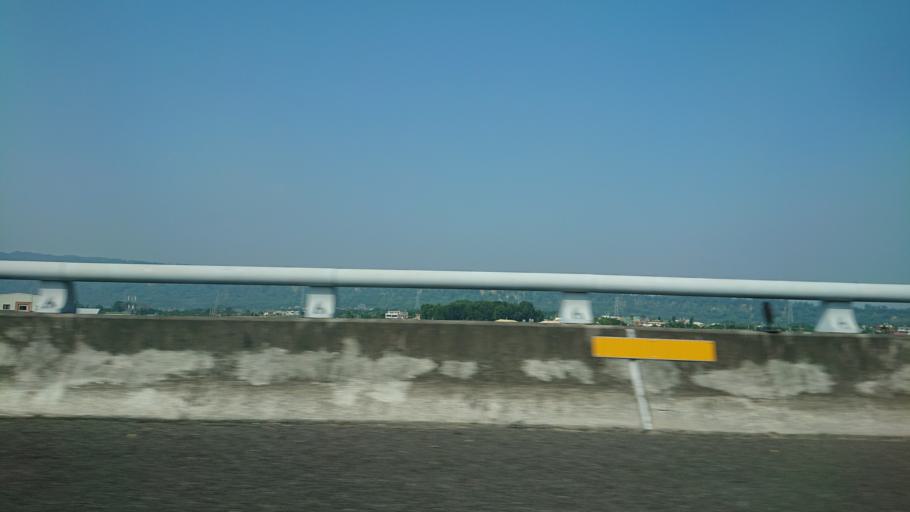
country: TW
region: Taiwan
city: Lugu
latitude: 23.8133
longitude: 120.6988
